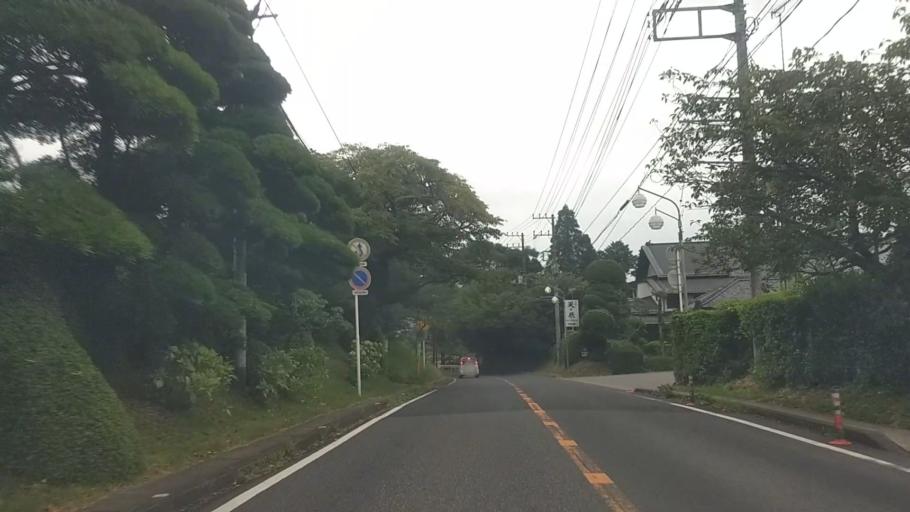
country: JP
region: Chiba
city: Kisarazu
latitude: 35.3012
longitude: 140.0732
